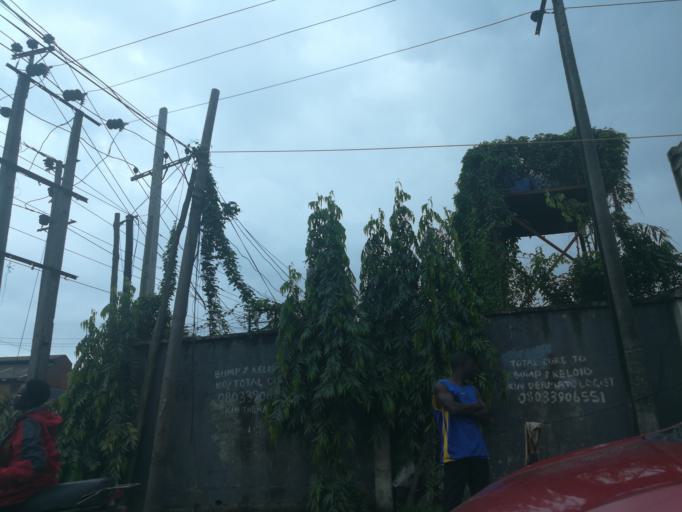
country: NG
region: Lagos
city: Agege
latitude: 6.6145
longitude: 3.3357
